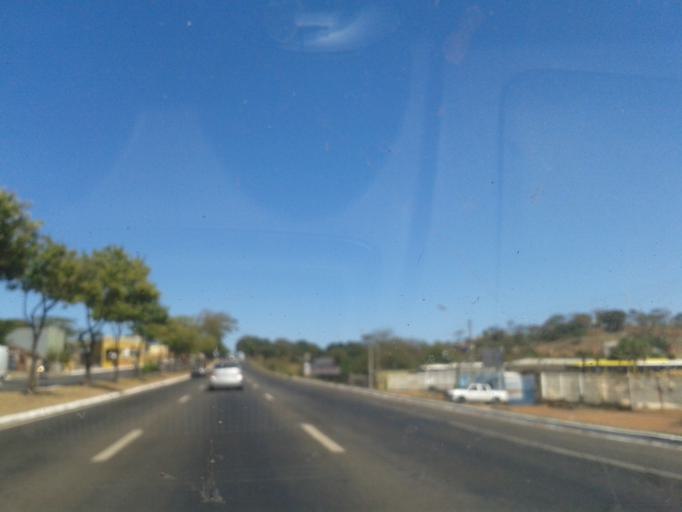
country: BR
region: Goias
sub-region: Goiania
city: Goiania
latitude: -16.6391
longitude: -49.2849
